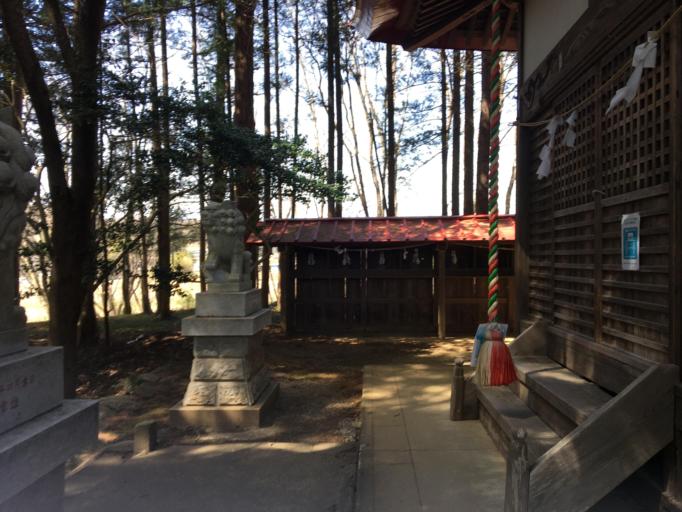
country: JP
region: Saitama
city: Sakado
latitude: 35.9916
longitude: 139.3359
